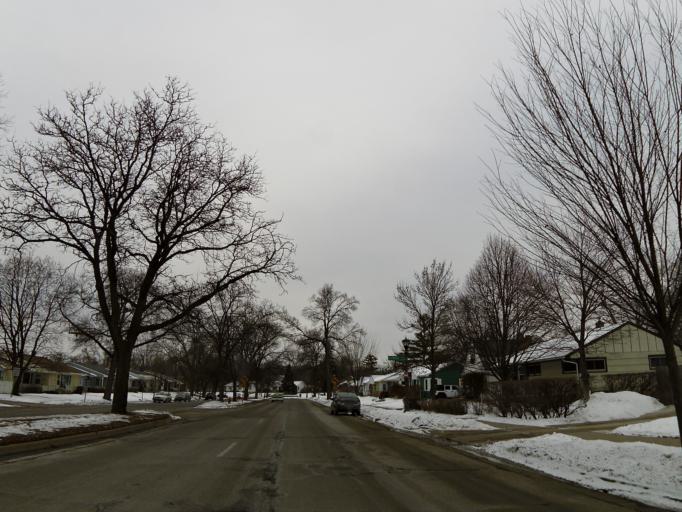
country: US
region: Minnesota
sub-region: Dakota County
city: Mendota Heights
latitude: 44.9055
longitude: -93.1794
